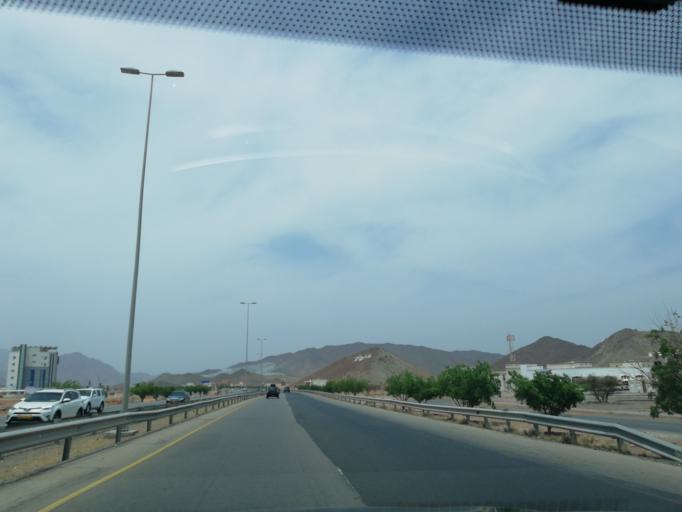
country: OM
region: Muhafazat ad Dakhiliyah
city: Bidbid
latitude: 23.4658
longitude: 58.1480
